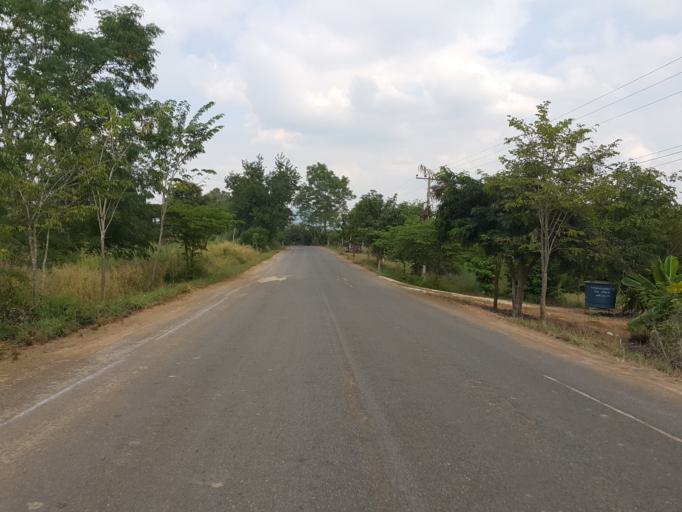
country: TH
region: Sukhothai
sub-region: Amphoe Si Satchanalai
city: Si Satchanalai
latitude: 17.4595
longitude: 99.6314
